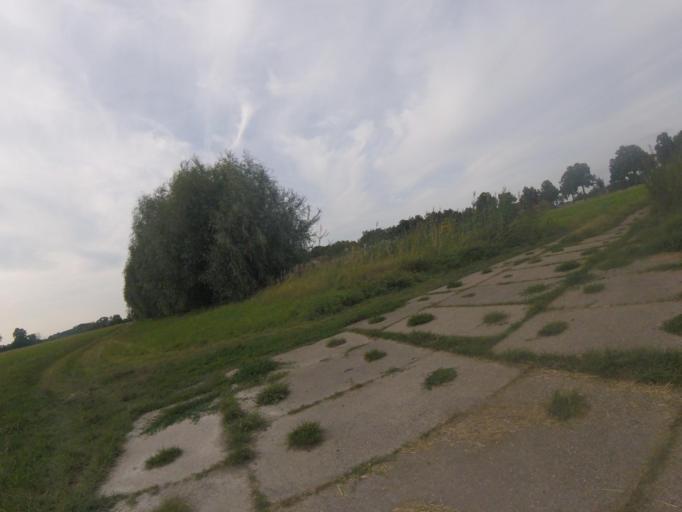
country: DE
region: Brandenburg
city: Rangsdorf
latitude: 52.3202
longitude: 13.4663
